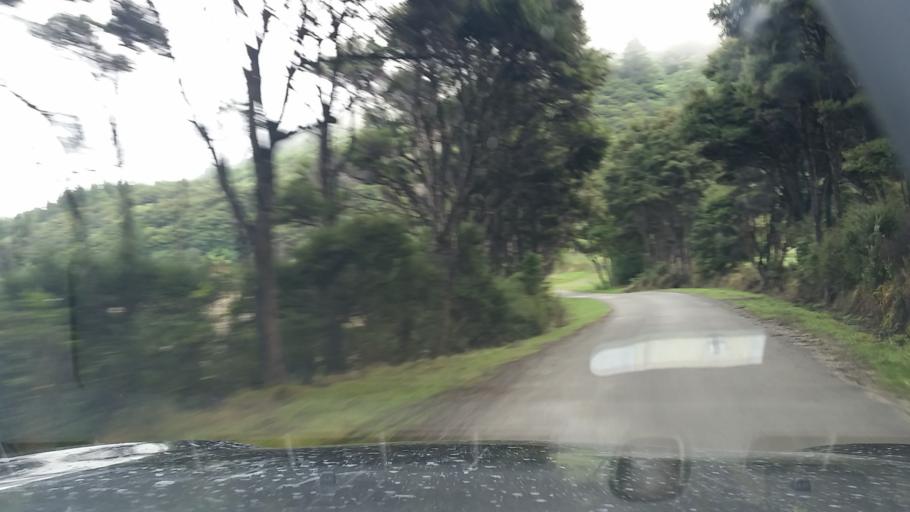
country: NZ
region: Marlborough
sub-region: Marlborough District
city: Picton
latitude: -41.1762
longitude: 174.0611
